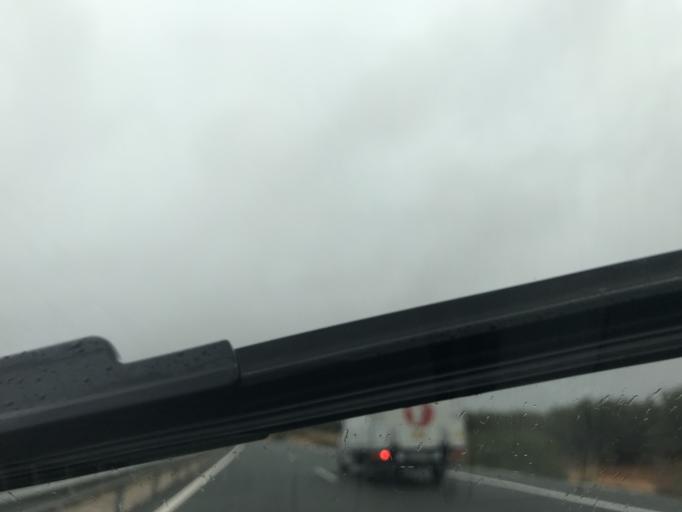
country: ES
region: Andalusia
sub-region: Provincia de Malaga
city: Mollina
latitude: 37.1266
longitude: -4.6800
